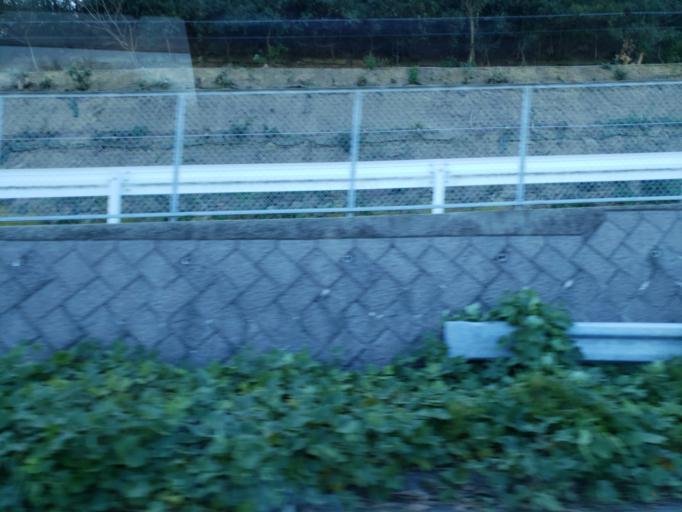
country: JP
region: Hyogo
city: Akashi
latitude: 34.5141
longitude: 134.8750
